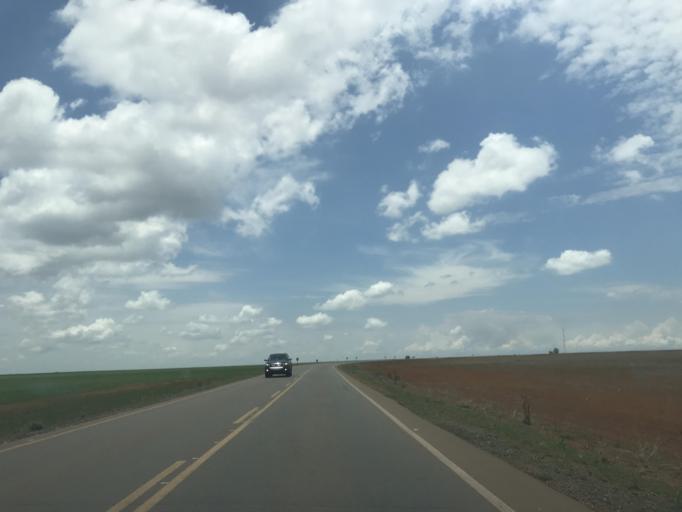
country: BR
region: Goias
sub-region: Vianopolis
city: Vianopolis
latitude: -16.5248
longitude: -48.2397
